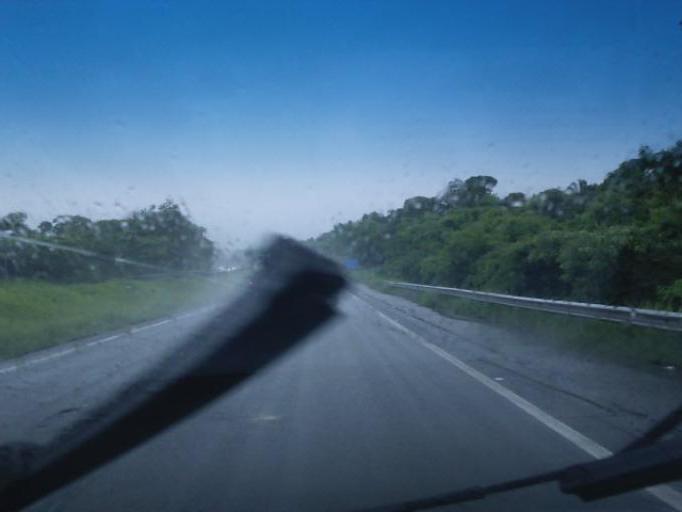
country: BR
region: Sao Paulo
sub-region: Pariquera-Acu
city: Pariquera Acu
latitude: -24.6484
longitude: -47.9255
